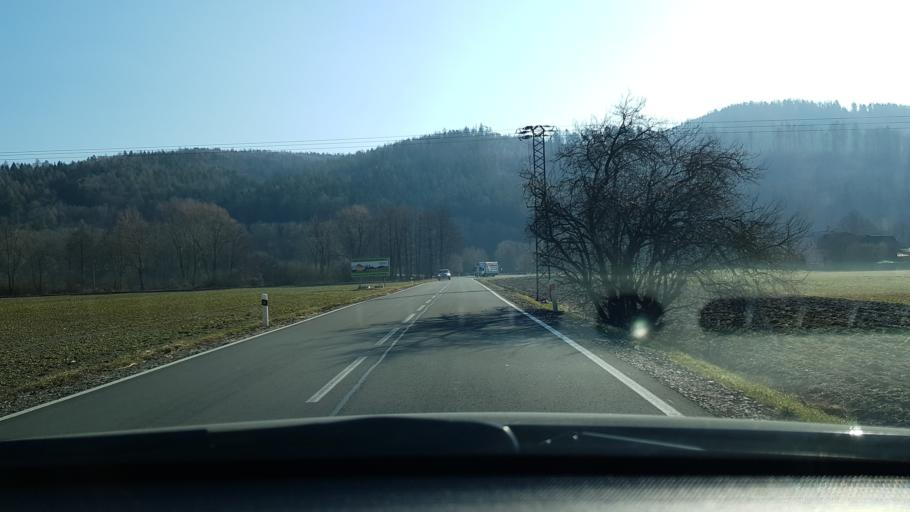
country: CZ
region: Olomoucky
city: Dolni Bohdikov
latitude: 49.9990
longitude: 16.8919
